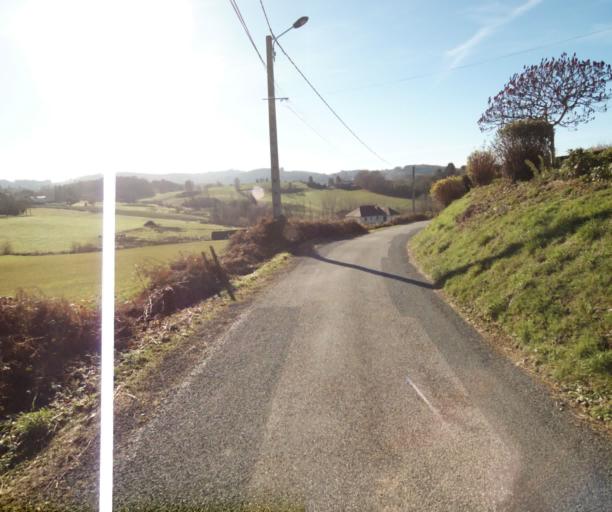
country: FR
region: Limousin
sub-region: Departement de la Correze
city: Sainte-Fortunade
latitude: 45.2253
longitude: 1.7649
